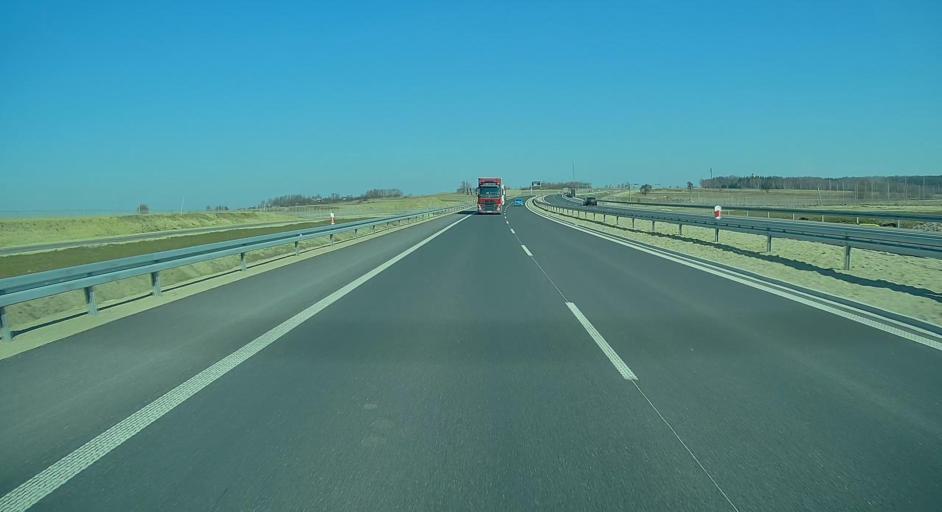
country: PL
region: Subcarpathian Voivodeship
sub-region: Powiat rzeszowski
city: Gorno
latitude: 50.2934
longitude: 22.1156
